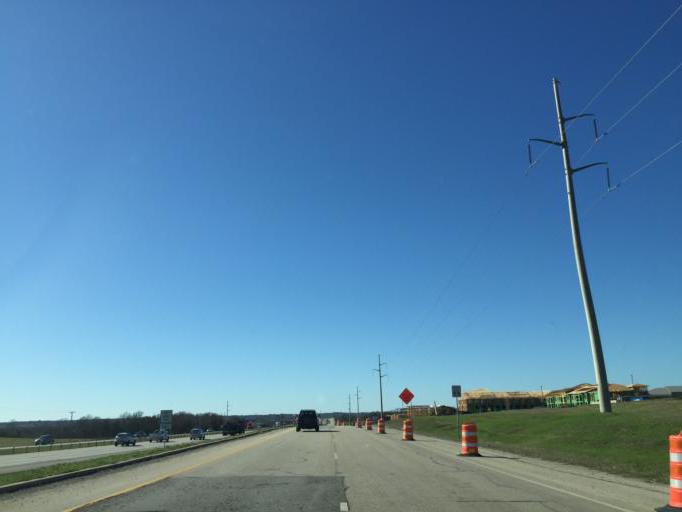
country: US
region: Texas
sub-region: Parker County
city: Hudson Oaks
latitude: 32.7525
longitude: -97.7146
